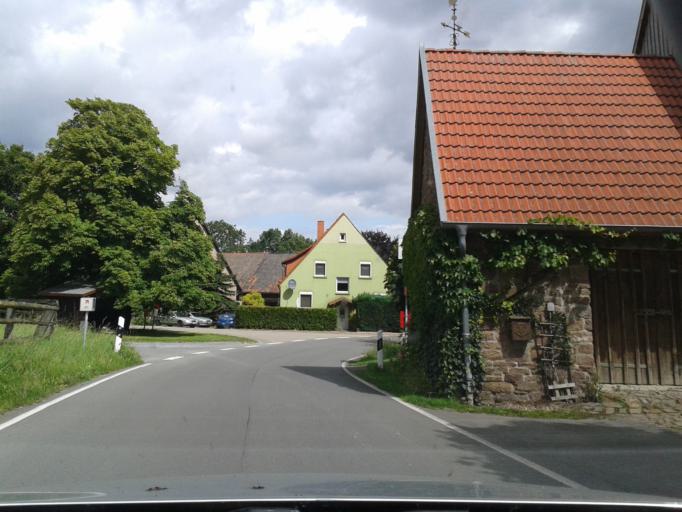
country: DE
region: North Rhine-Westphalia
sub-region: Regierungsbezirk Detmold
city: Dorentrup
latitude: 52.0151
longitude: 9.0446
